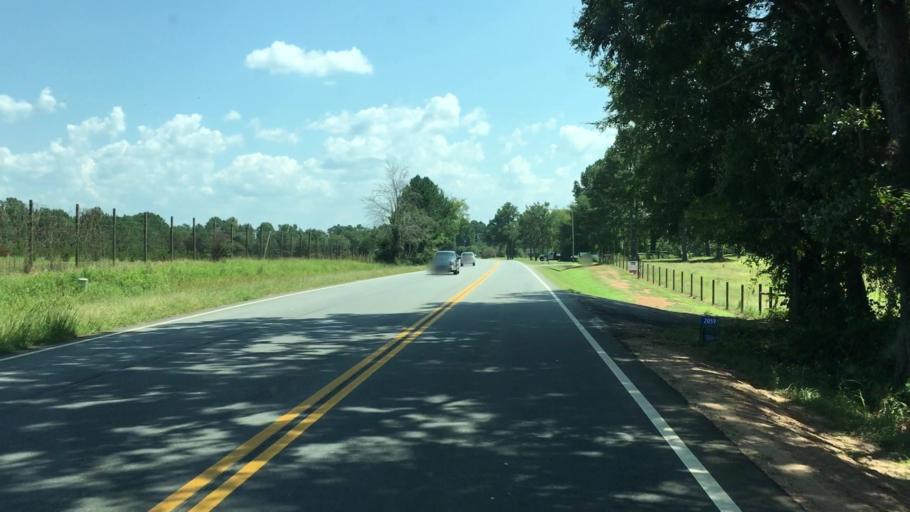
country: US
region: Georgia
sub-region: Oconee County
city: Watkinsville
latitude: 33.7453
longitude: -83.4325
